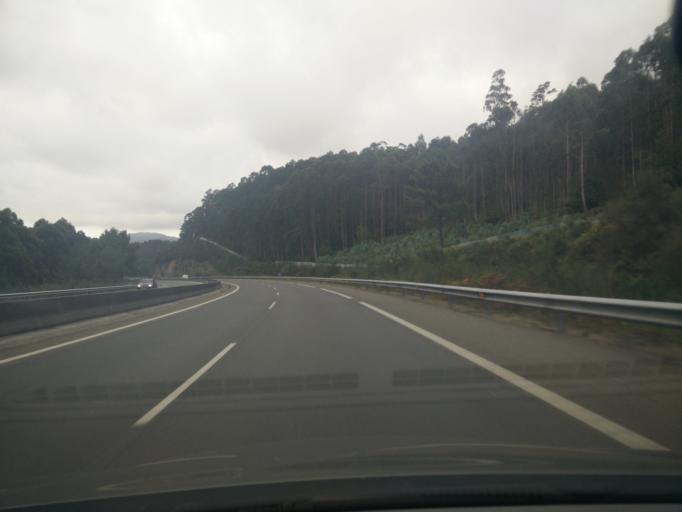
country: ES
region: Galicia
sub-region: Provincia da Coruna
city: Arteixo
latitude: 43.2822
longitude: -8.5105
